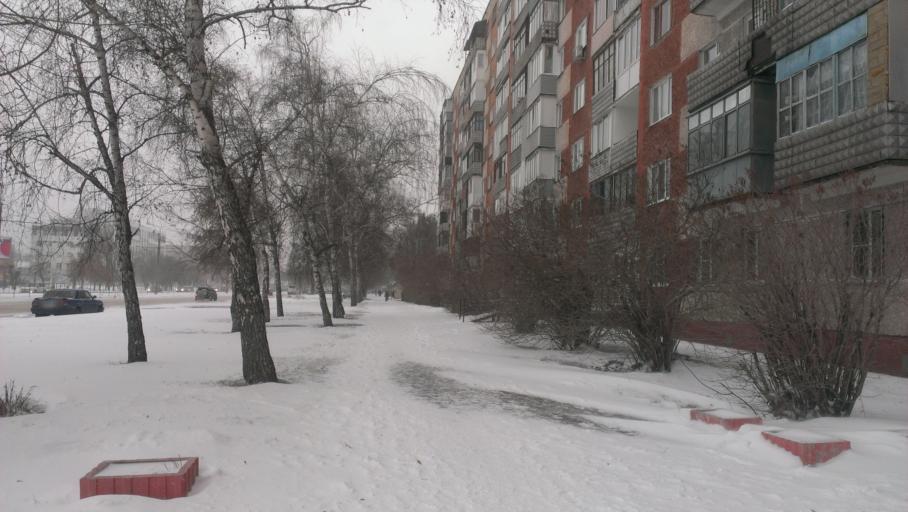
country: RU
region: Altai Krai
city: Novosilikatnyy
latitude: 53.3673
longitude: 83.6774
